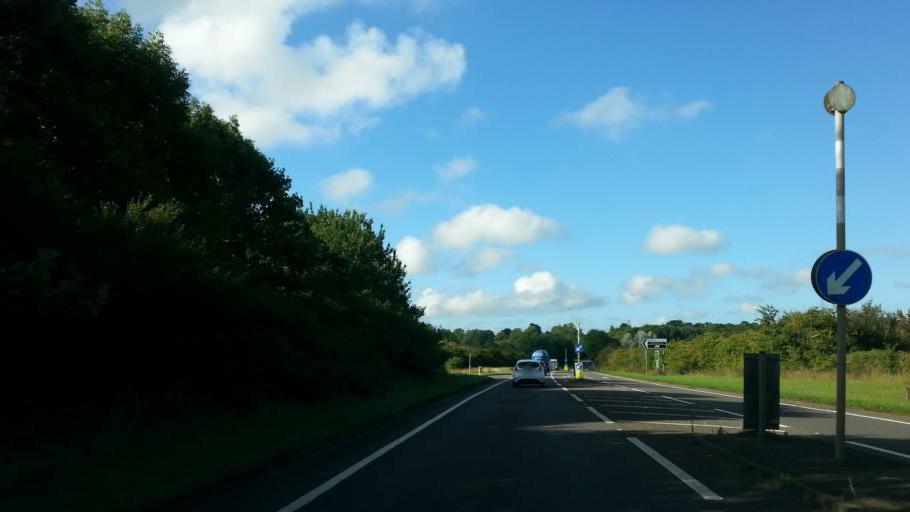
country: GB
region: England
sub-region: District of Rutland
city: South Luffenham
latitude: 52.5441
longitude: -0.5857
